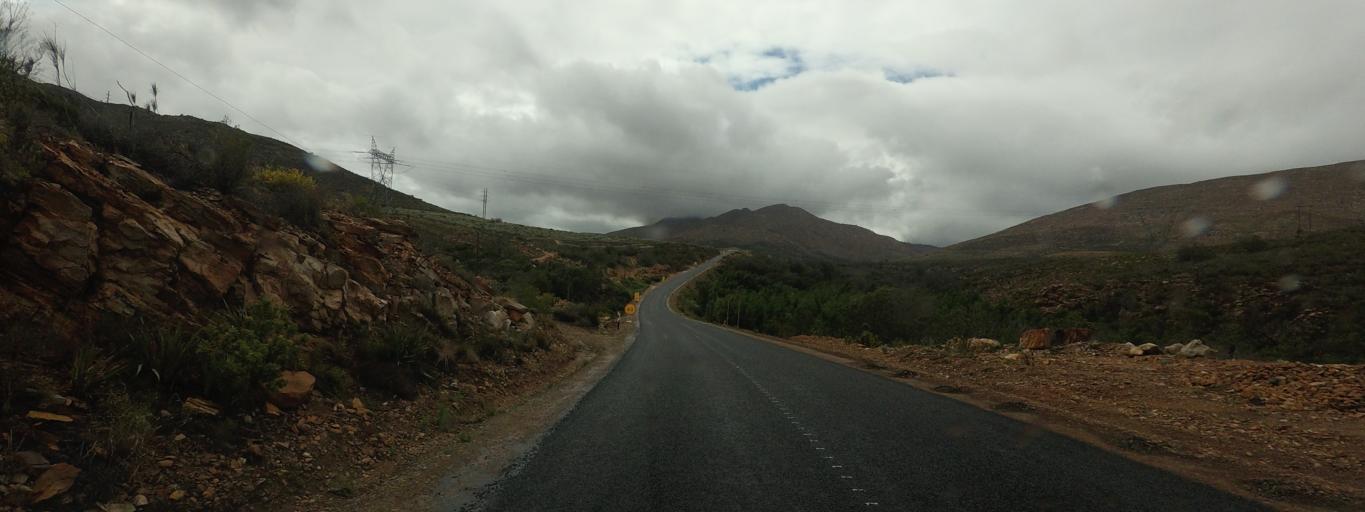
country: ZA
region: Western Cape
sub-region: Eden District Municipality
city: George
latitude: -33.8057
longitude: 22.3355
